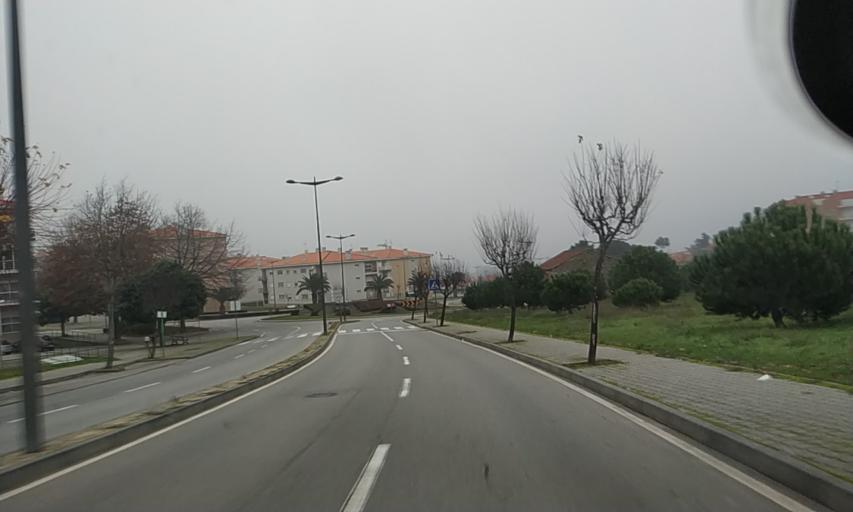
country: PT
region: Viseu
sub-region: Lamego
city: Lamego
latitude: 41.1074
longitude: -7.8067
